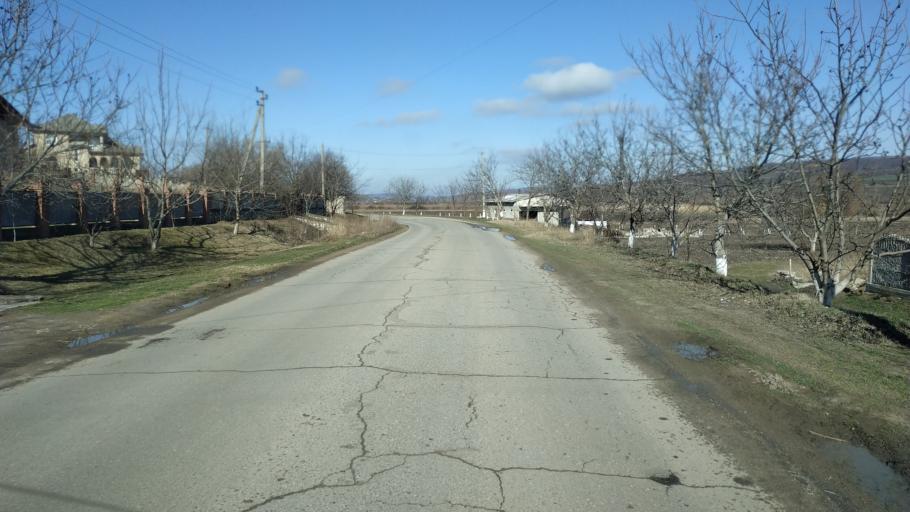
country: MD
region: Hincesti
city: Hincesti
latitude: 46.9370
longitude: 28.6372
